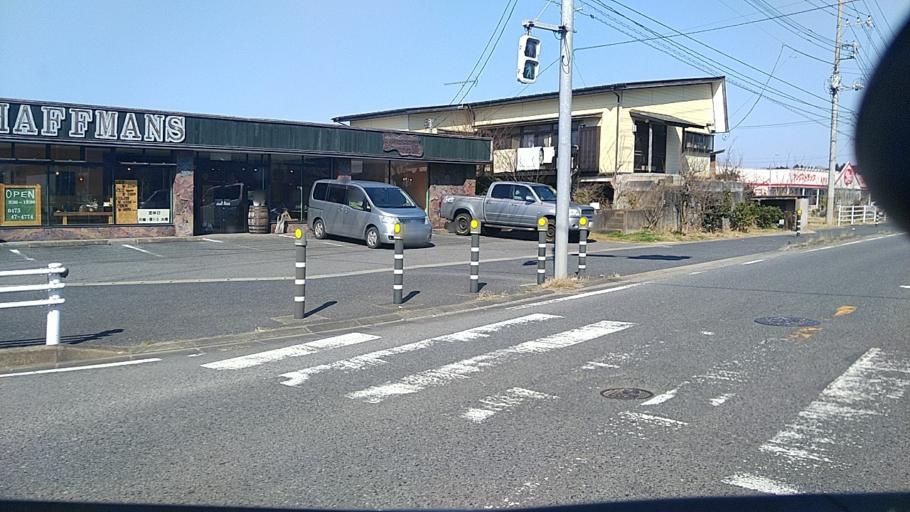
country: JP
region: Chiba
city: Mobara
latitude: 35.4048
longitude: 140.2378
